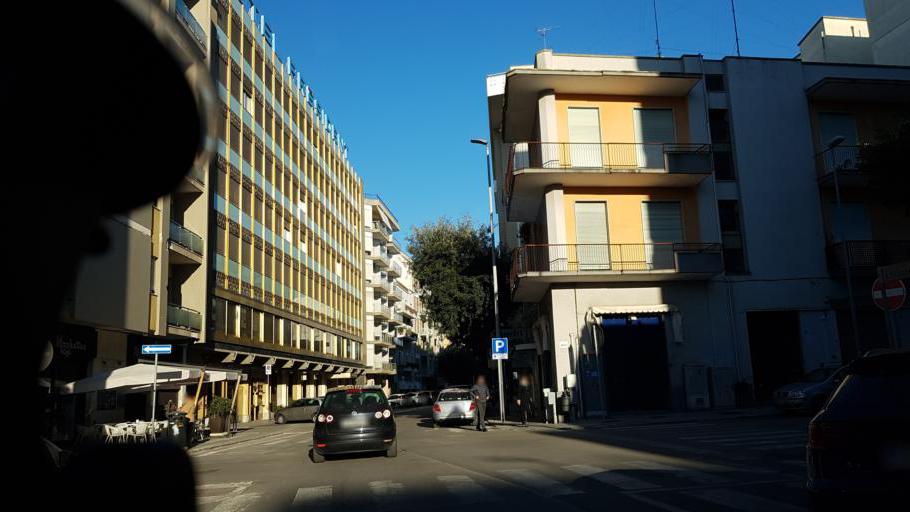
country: IT
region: Apulia
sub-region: Provincia di Lecce
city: Lecce
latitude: 40.3541
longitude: 18.1827
